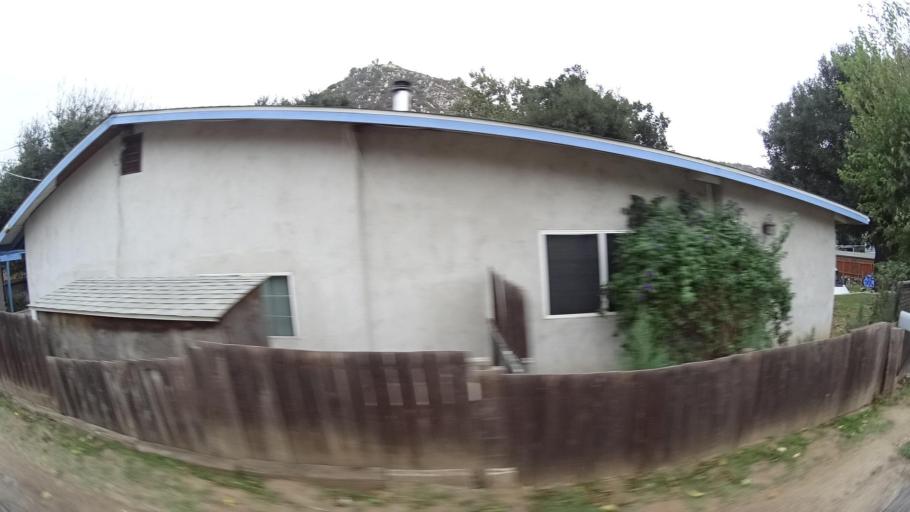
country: US
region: California
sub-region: San Diego County
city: Harbison Canyon
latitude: 32.8180
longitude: -116.8324
